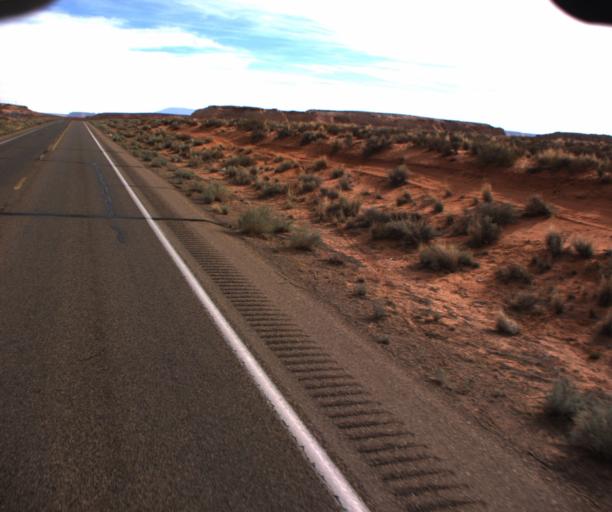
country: US
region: Arizona
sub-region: Coconino County
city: Page
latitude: 36.8927
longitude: -111.4669
